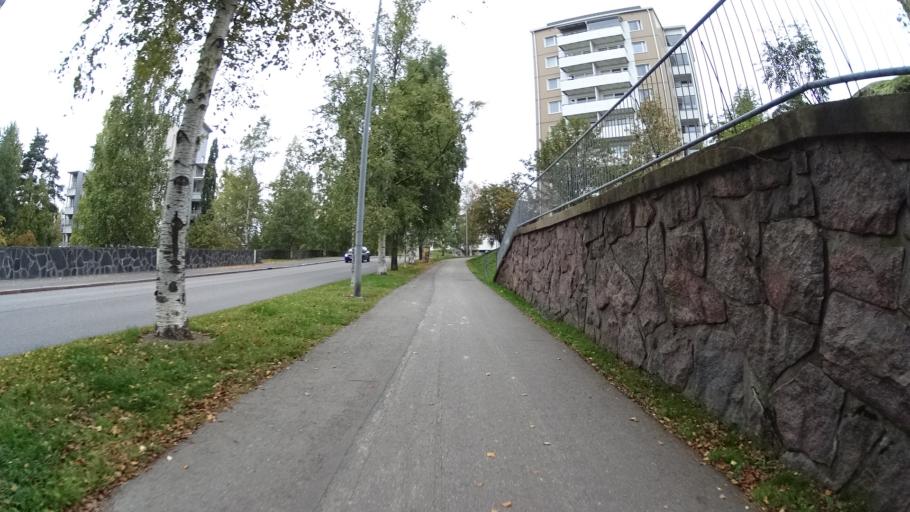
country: FI
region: Uusimaa
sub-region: Helsinki
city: Vantaa
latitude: 60.2138
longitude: 25.0408
